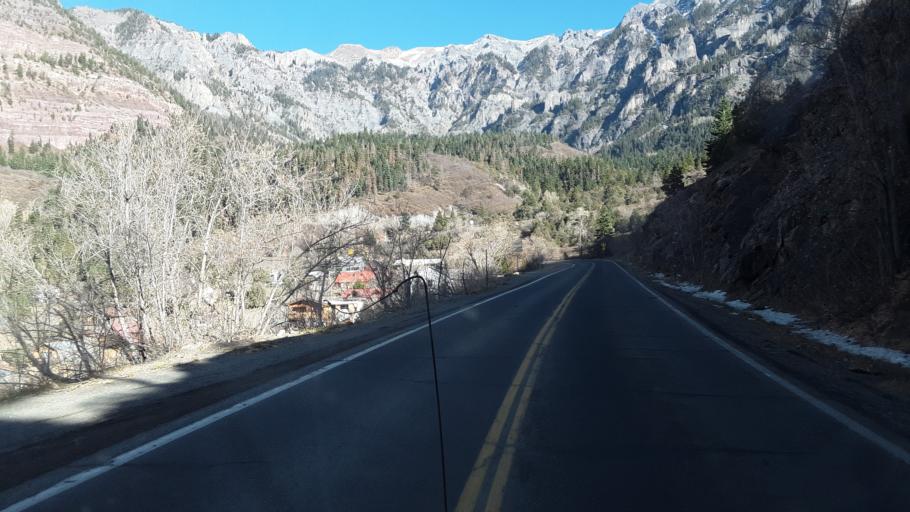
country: US
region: Colorado
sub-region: Ouray County
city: Ouray
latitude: 38.0178
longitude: -107.6709
